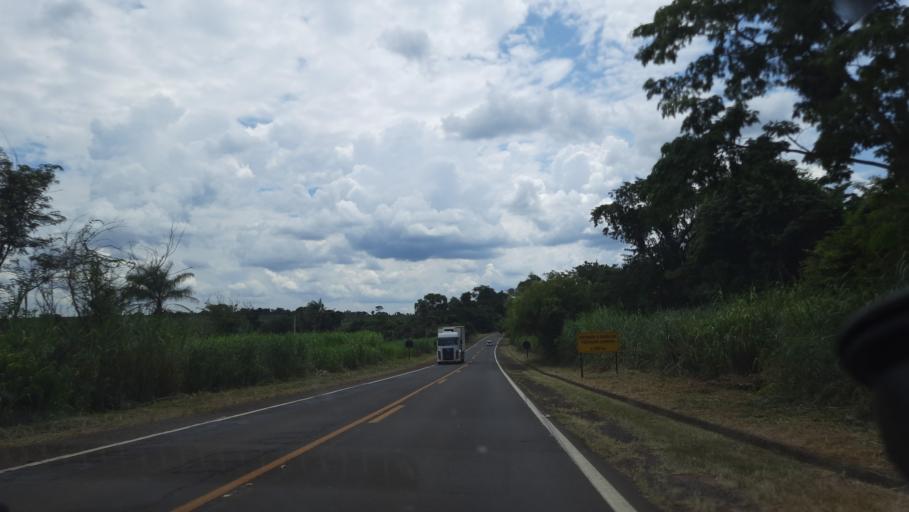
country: BR
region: Sao Paulo
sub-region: Mococa
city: Mococa
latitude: -21.4949
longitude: -47.0700
